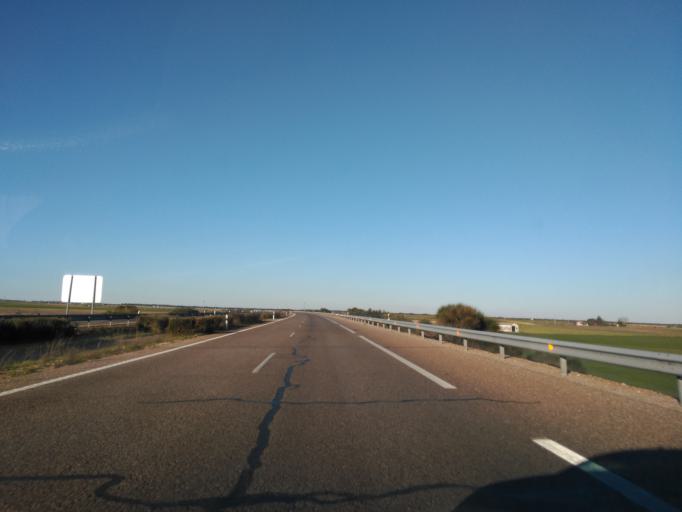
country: ES
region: Castille and Leon
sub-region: Provincia de Salamanca
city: Pajares de la Laguna
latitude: 41.1036
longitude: -5.4952
